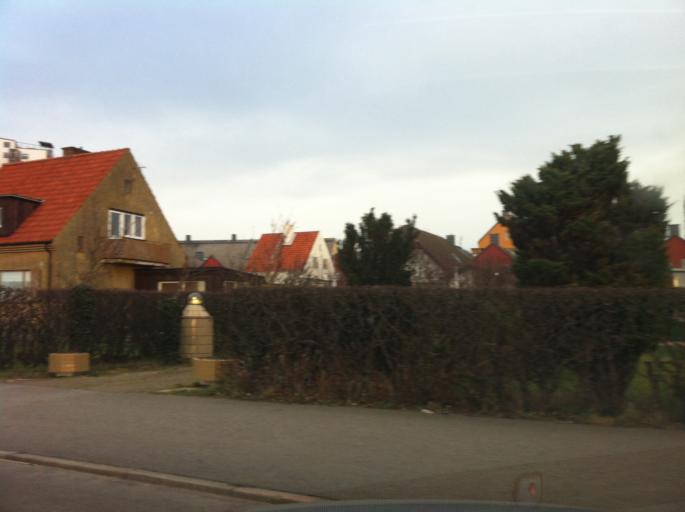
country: SE
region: Skane
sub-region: Hoganas Kommun
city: Hoganas
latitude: 56.1981
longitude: 12.5545
